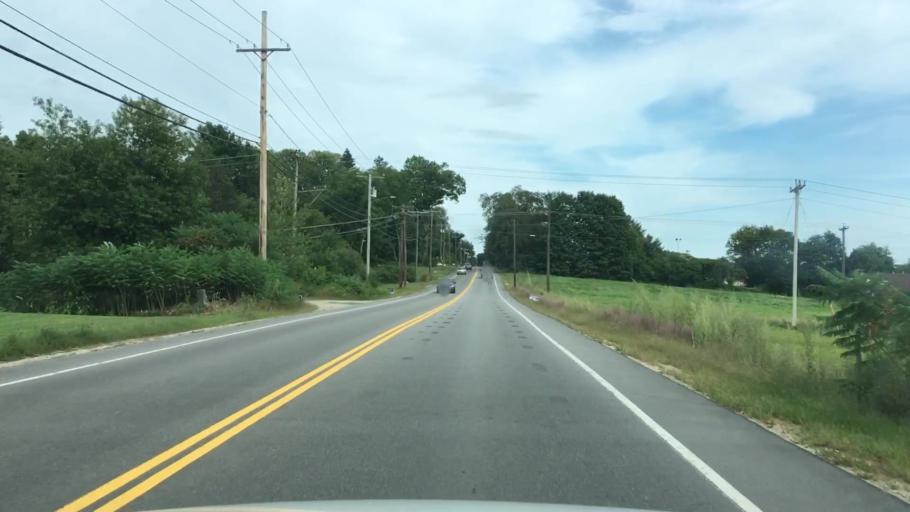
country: US
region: New Hampshire
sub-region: Strafford County
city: Madbury
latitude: 43.1881
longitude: -70.9101
